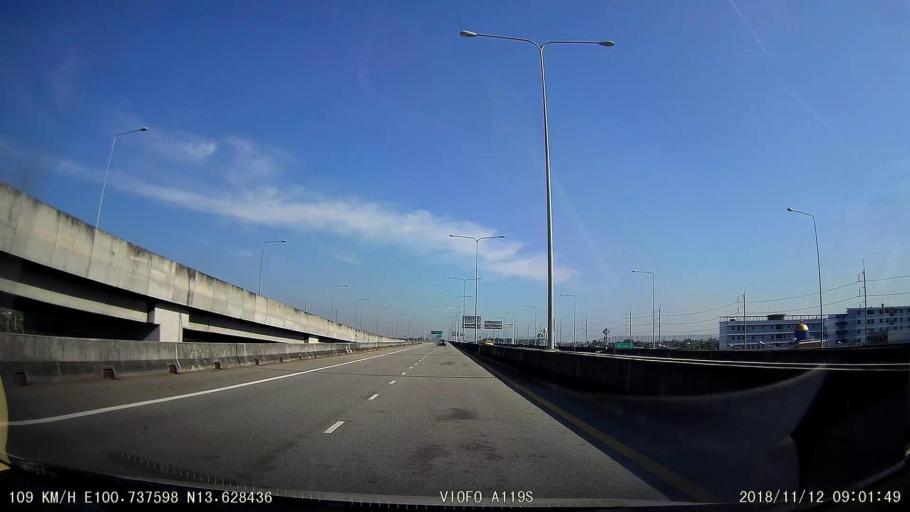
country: TH
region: Samut Prakan
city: Bang Bo District
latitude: 13.6287
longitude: 100.7393
